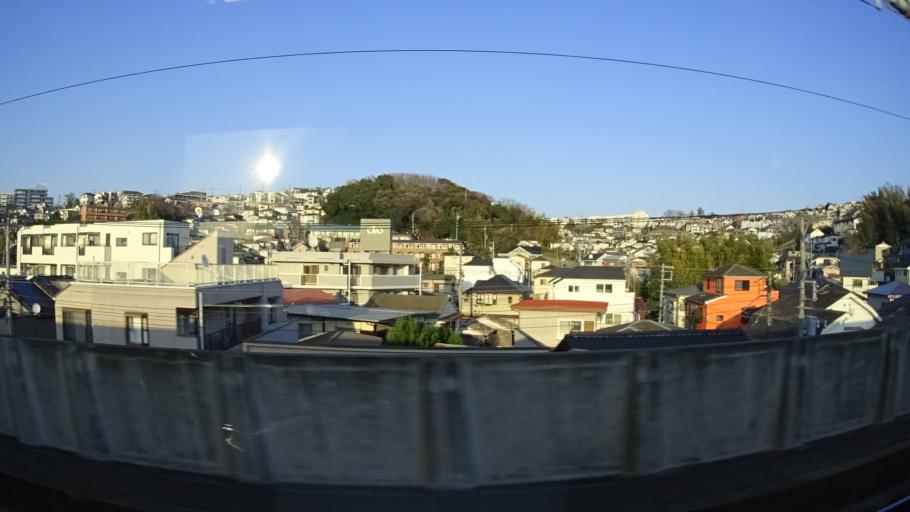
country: JP
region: Kanagawa
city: Yokohama
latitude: 35.4043
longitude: 139.5975
